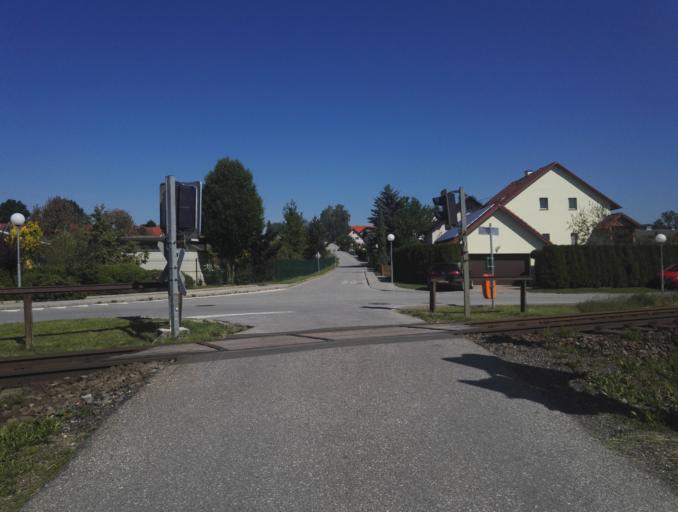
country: AT
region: Styria
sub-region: Politischer Bezirk Graz-Umgebung
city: Raaba
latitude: 47.0317
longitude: 15.5003
